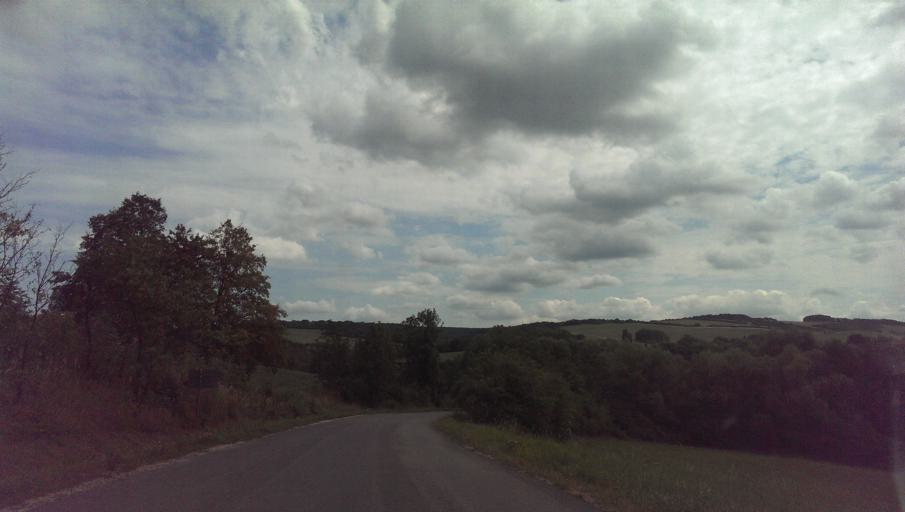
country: CZ
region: Zlin
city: Dolni Nemci
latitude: 48.9271
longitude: 17.5558
